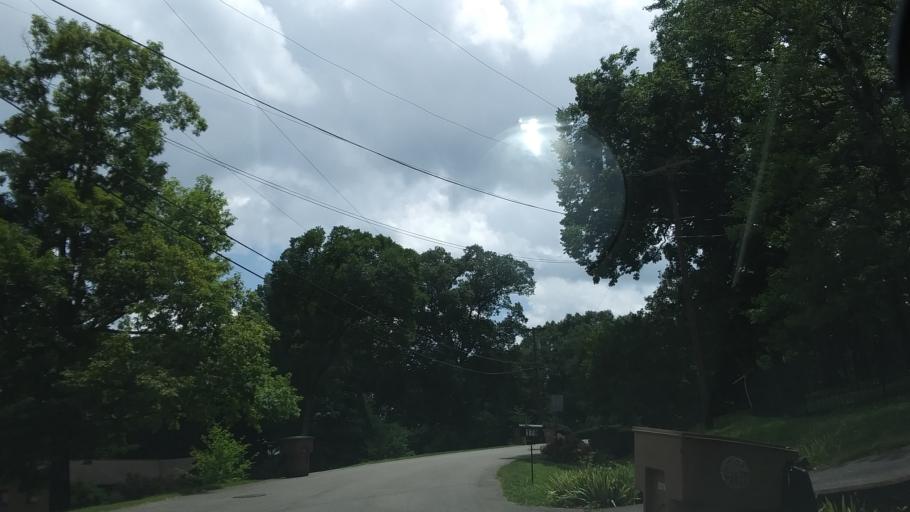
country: US
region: Tennessee
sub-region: Davidson County
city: Belle Meade
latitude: 36.1365
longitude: -86.8637
